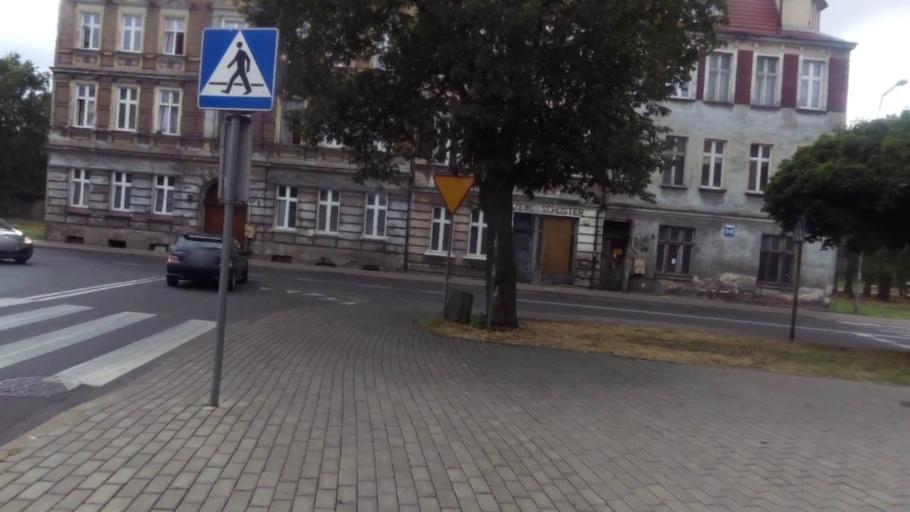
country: PL
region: Lubusz
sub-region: Powiat gorzowski
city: Kostrzyn nad Odra
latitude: 52.5910
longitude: 14.6439
